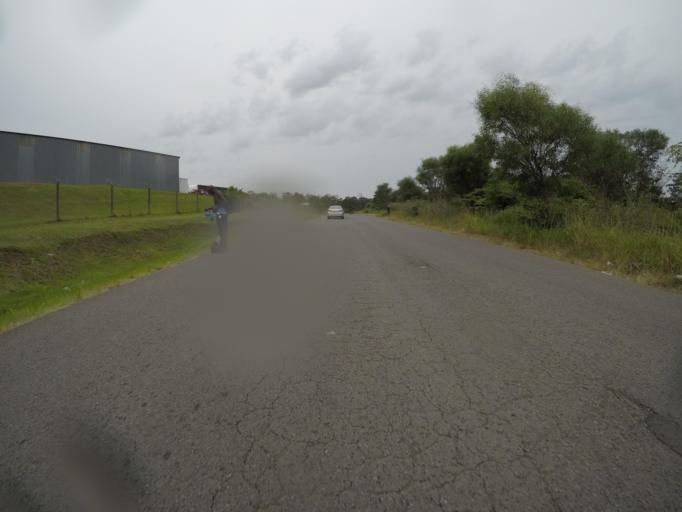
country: ZA
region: Eastern Cape
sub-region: Buffalo City Metropolitan Municipality
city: East London
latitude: -32.9866
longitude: 27.8265
